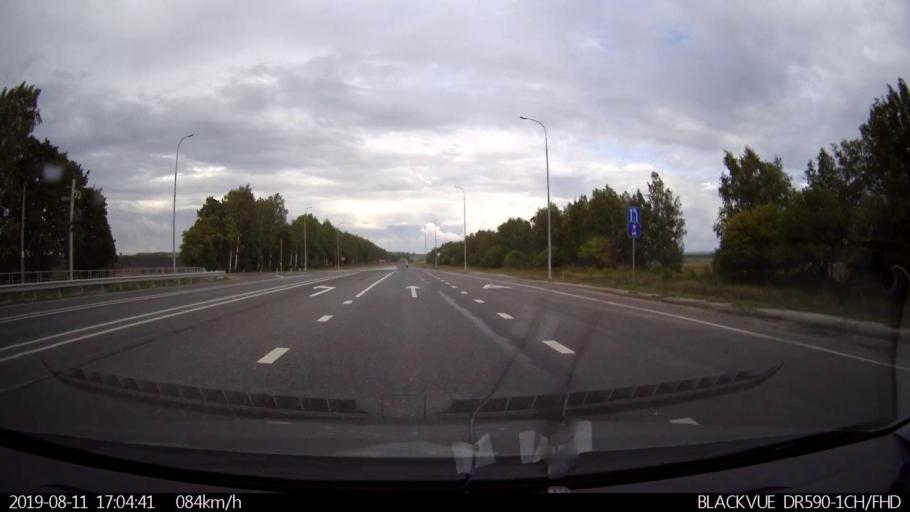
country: RU
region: Ulyanovsk
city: Mayna
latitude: 54.3002
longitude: 47.7695
